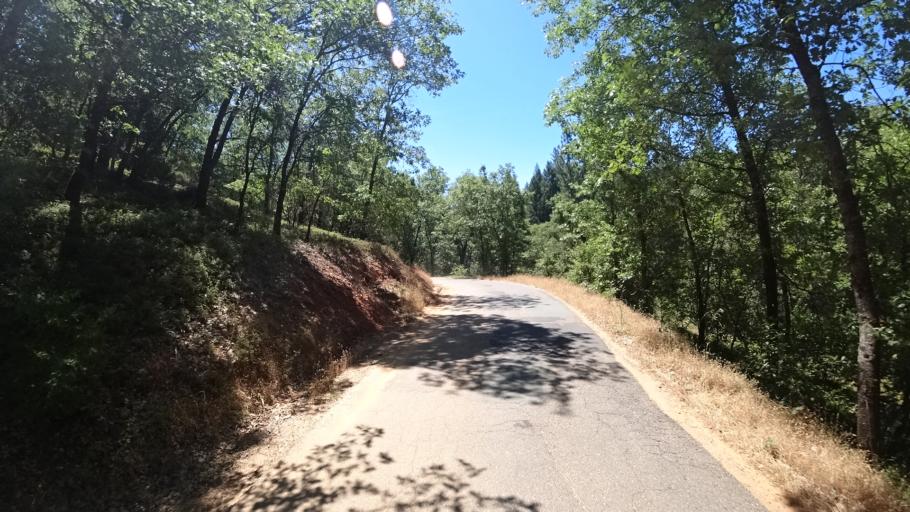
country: US
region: California
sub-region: Amador County
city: Pioneer
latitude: 38.4118
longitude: -120.5245
